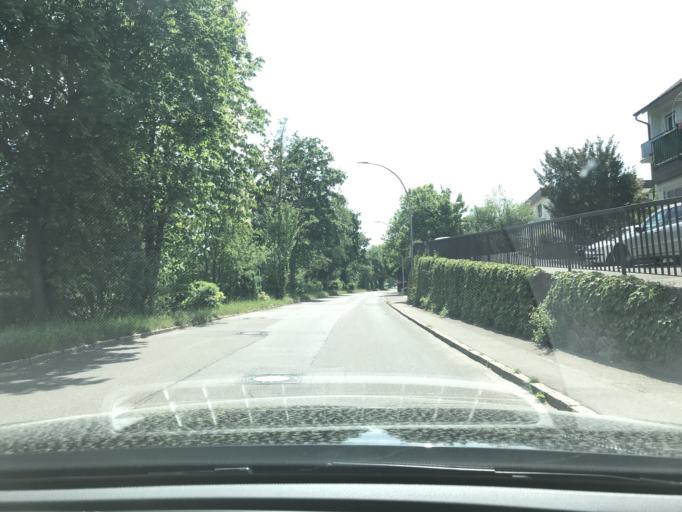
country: DE
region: Baden-Wuerttemberg
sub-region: Regierungsbezirk Stuttgart
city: Weinstadt-Endersbach
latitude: 48.8102
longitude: 9.3591
